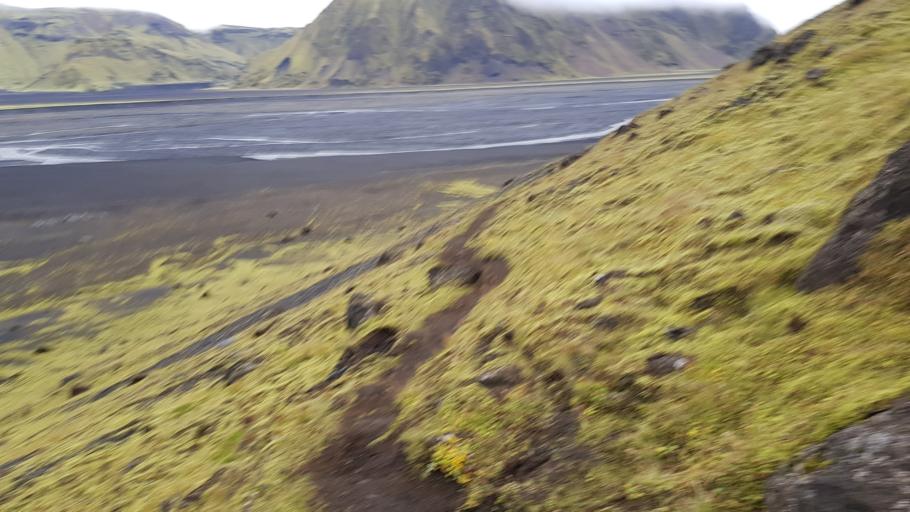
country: IS
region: South
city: Vestmannaeyjar
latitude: 63.5315
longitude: -18.8518
